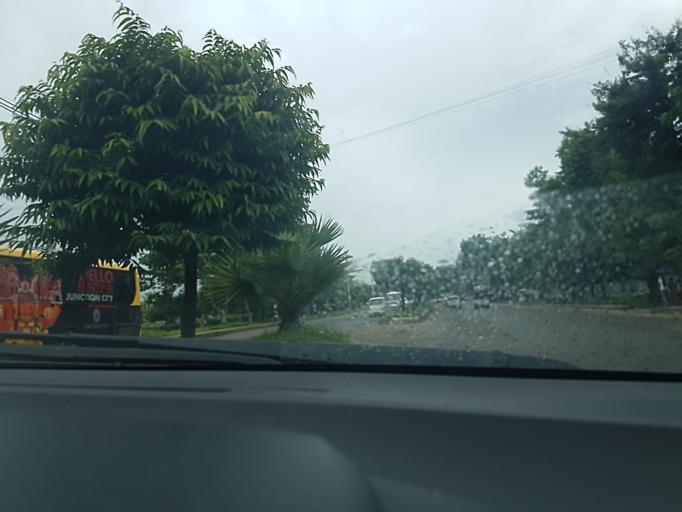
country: MM
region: Yangon
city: Yangon
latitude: 17.0373
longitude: 96.1313
